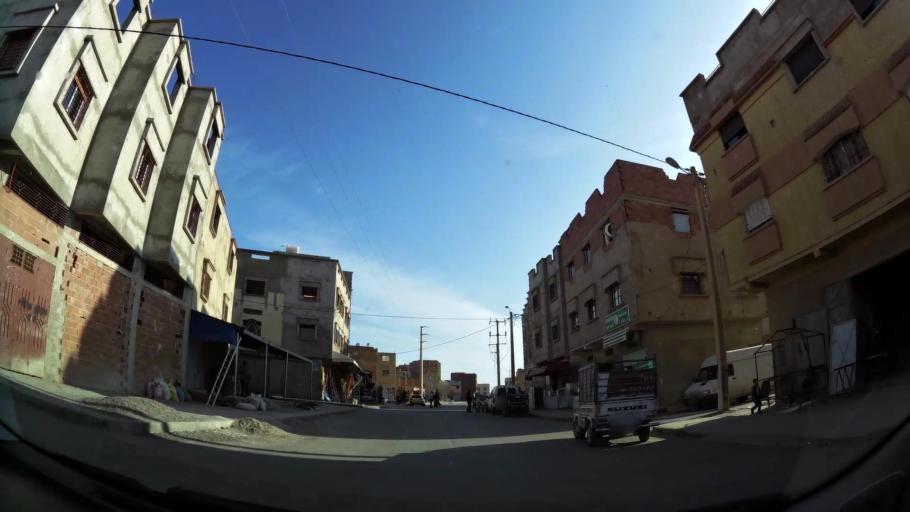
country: MA
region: Oriental
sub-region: Oujda-Angad
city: Oujda
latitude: 34.7130
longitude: -1.8990
